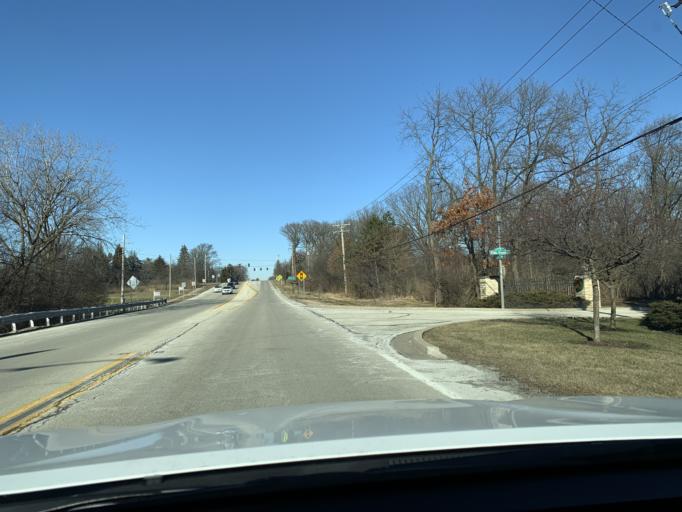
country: US
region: Illinois
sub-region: DuPage County
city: Burr Ridge
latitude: 41.7437
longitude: -87.9153
